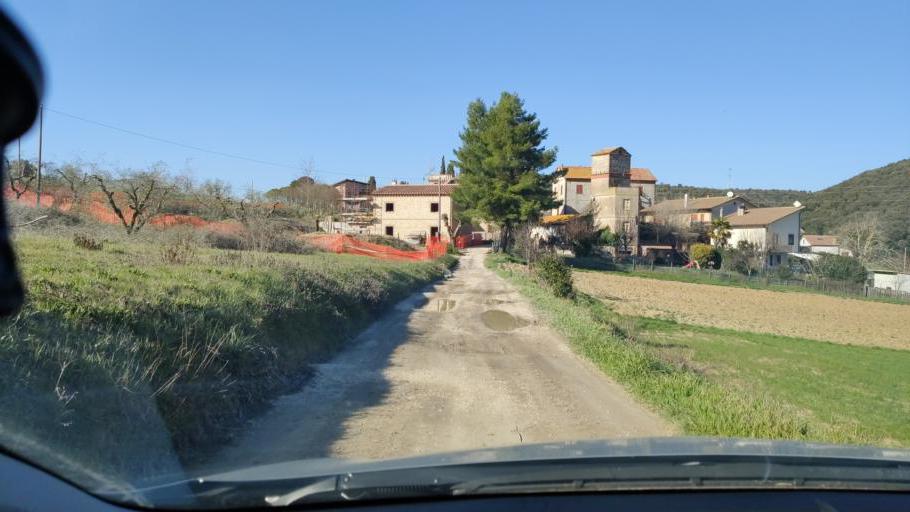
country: IT
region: Umbria
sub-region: Provincia di Terni
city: Fornole
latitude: 42.5619
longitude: 12.4490
